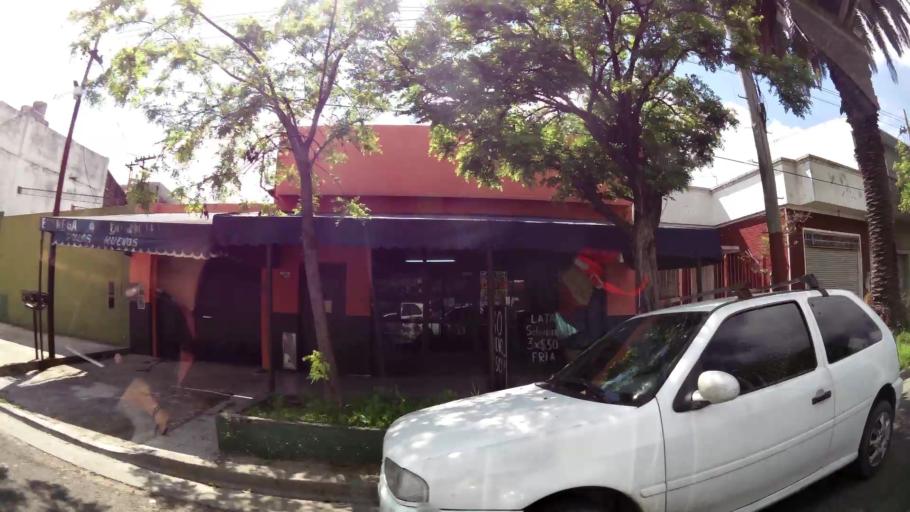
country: AR
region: Buenos Aires
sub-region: Partido de Lanus
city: Lanus
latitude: -34.6756
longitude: -58.4150
